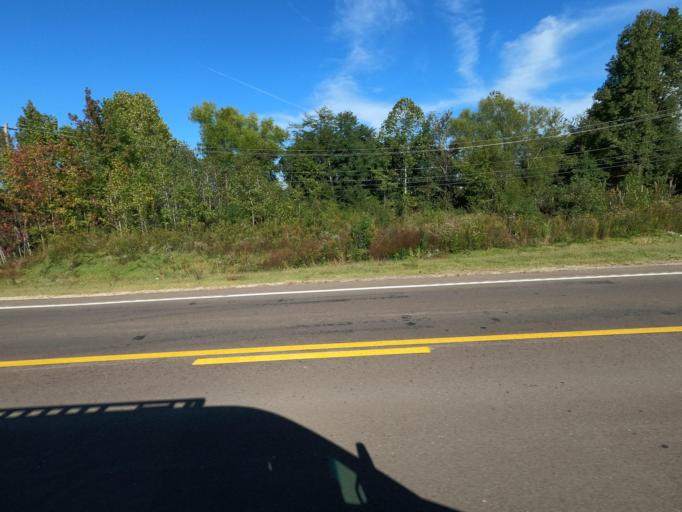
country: US
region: Tennessee
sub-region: Shelby County
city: Arlington
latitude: 35.2595
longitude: -89.6625
